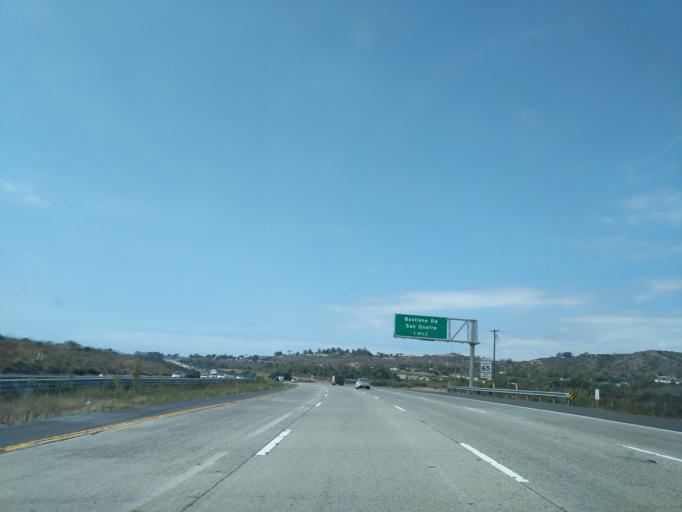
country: US
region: California
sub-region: Orange County
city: San Clemente
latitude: 33.3775
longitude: -117.5639
